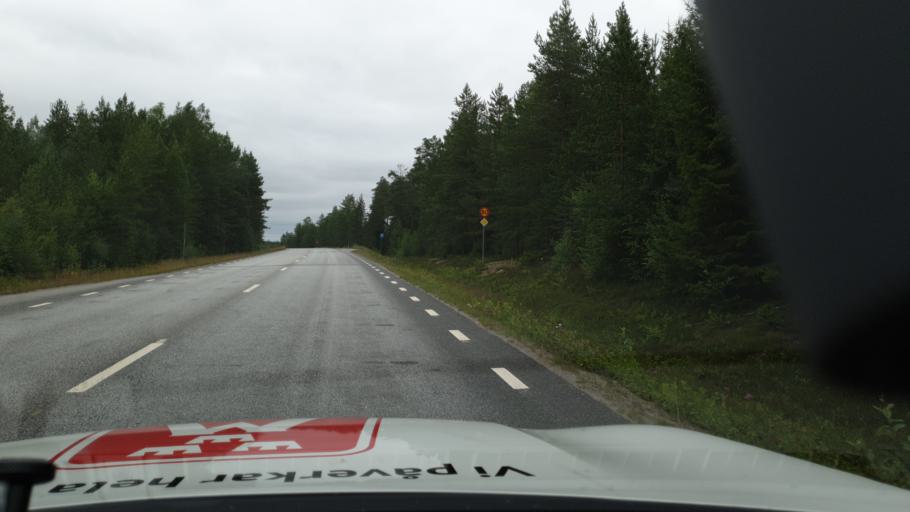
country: SE
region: Vaesterbotten
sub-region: Umea Kommun
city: Ersmark
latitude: 63.8936
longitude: 20.3128
